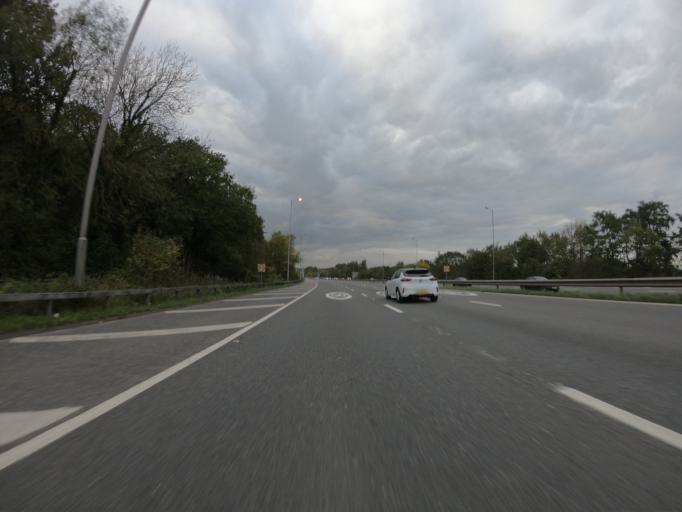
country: GB
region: England
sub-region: Greater London
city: Bexley
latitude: 51.4431
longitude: 0.1668
